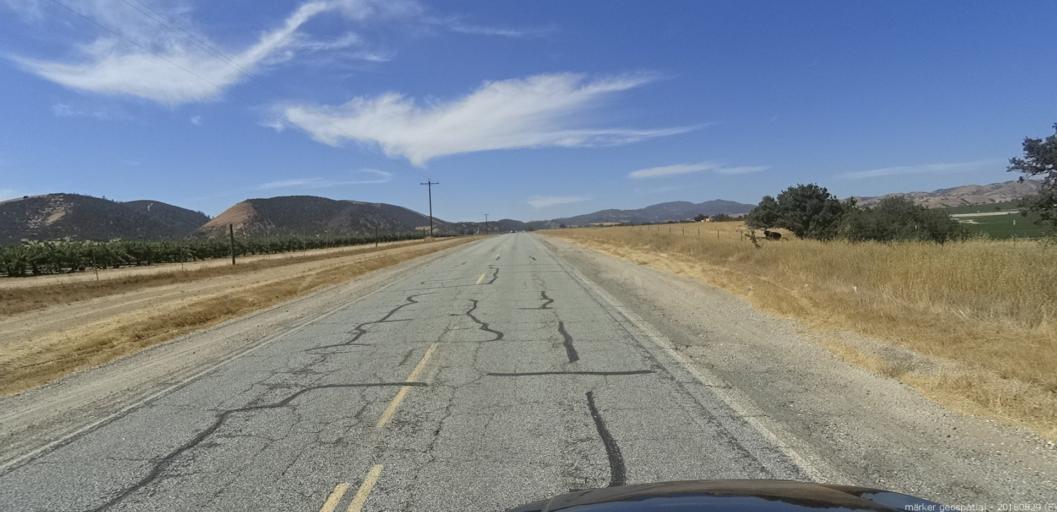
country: US
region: California
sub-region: San Luis Obispo County
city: Lake Nacimiento
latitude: 35.8794
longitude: -120.8980
